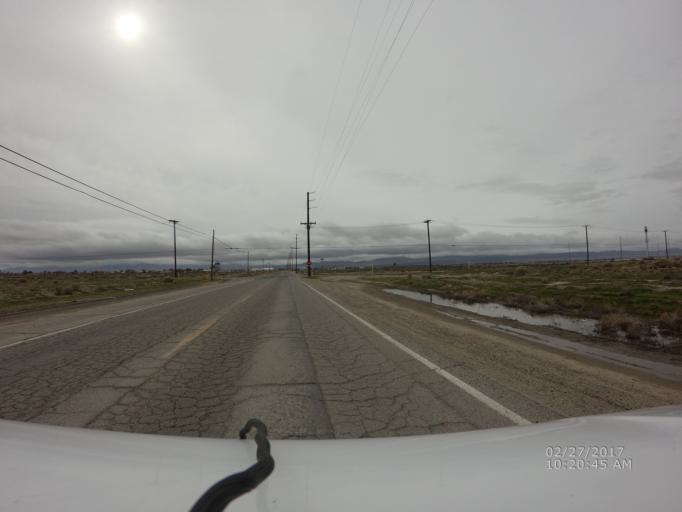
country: US
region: California
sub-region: Los Angeles County
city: Lancaster
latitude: 34.7340
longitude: -118.1308
